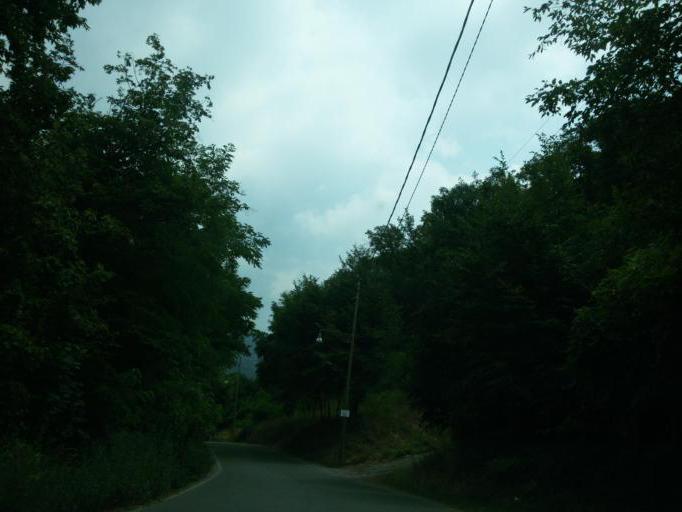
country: IT
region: Liguria
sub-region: Provincia di Genova
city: Piccarello
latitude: 44.4340
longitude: 9.0152
